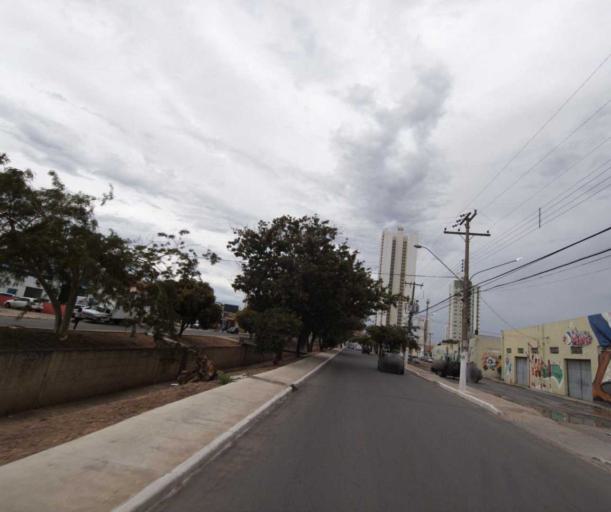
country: BR
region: Mato Grosso
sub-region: Cuiaba
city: Cuiaba
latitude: -15.6174
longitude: -56.0764
